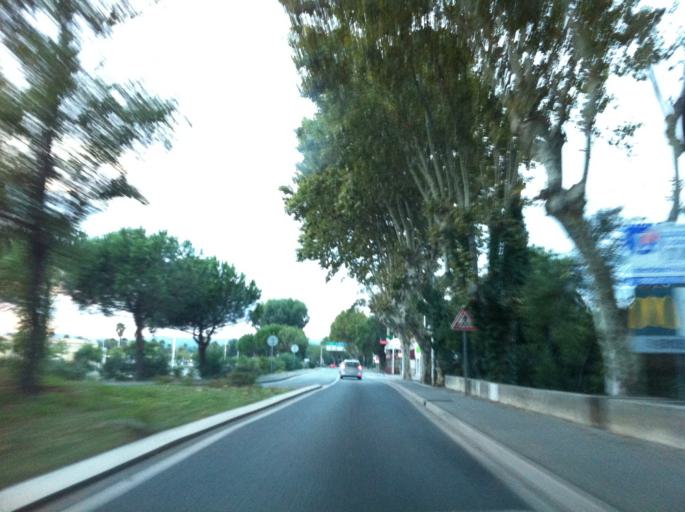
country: FR
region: Provence-Alpes-Cote d'Azur
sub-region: Departement du Var
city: Gassin
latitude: 43.2631
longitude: 6.5819
